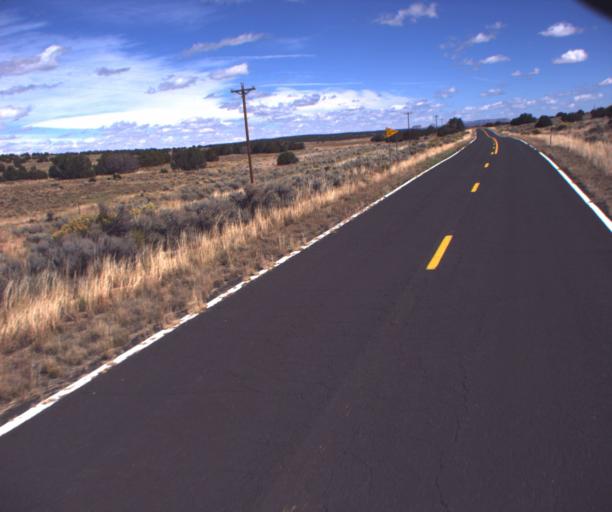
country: US
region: New Mexico
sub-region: McKinley County
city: Zuni Pueblo
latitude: 34.9943
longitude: -109.0981
